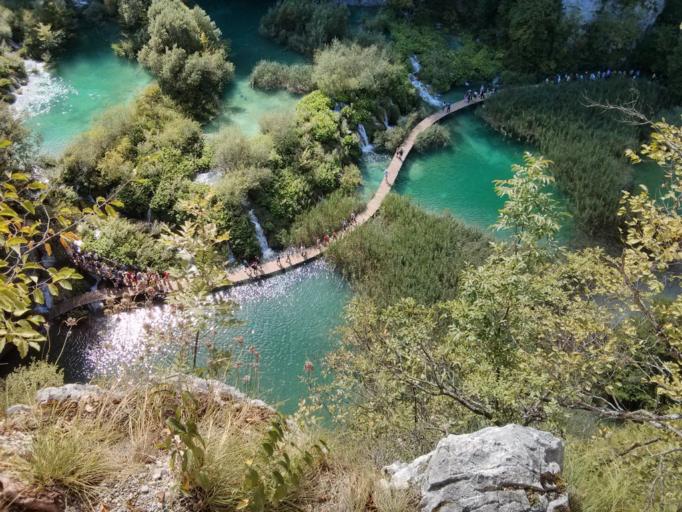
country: HR
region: Licko-Senjska
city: Jezerce
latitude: 44.9002
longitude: 15.6118
